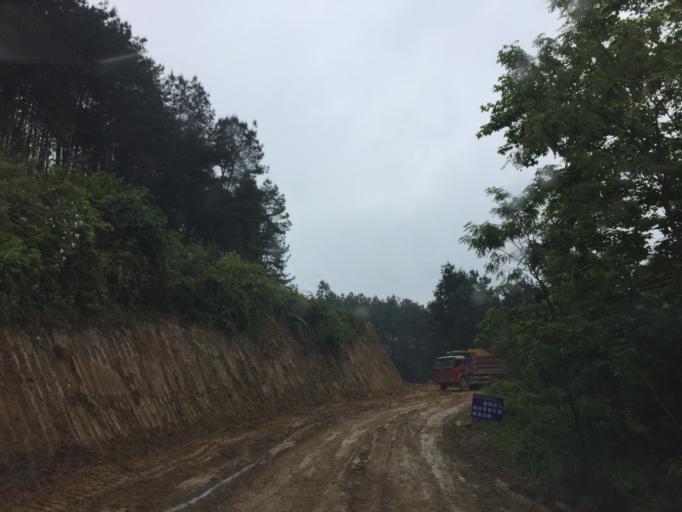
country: CN
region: Guizhou Sheng
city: Kuanping
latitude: 28.0258
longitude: 108.0528
